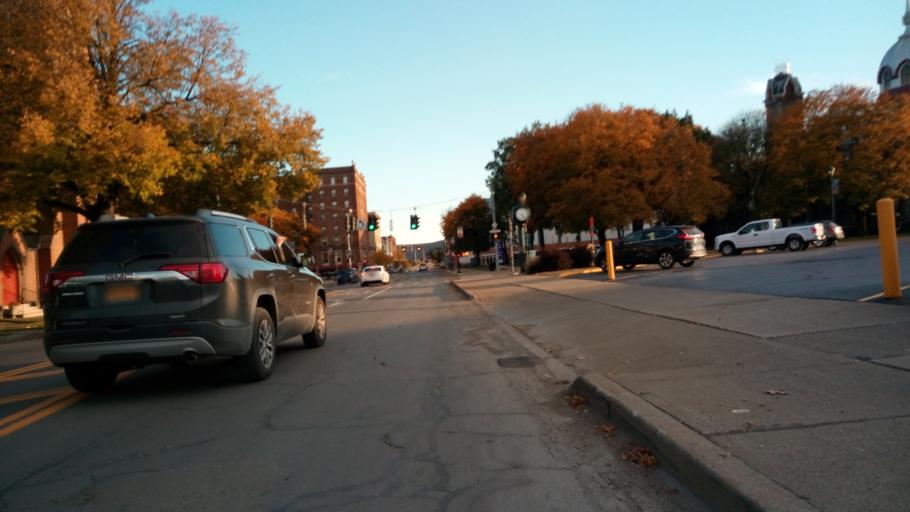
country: US
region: New York
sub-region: Chemung County
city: Elmira
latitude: 42.0903
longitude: -76.8086
